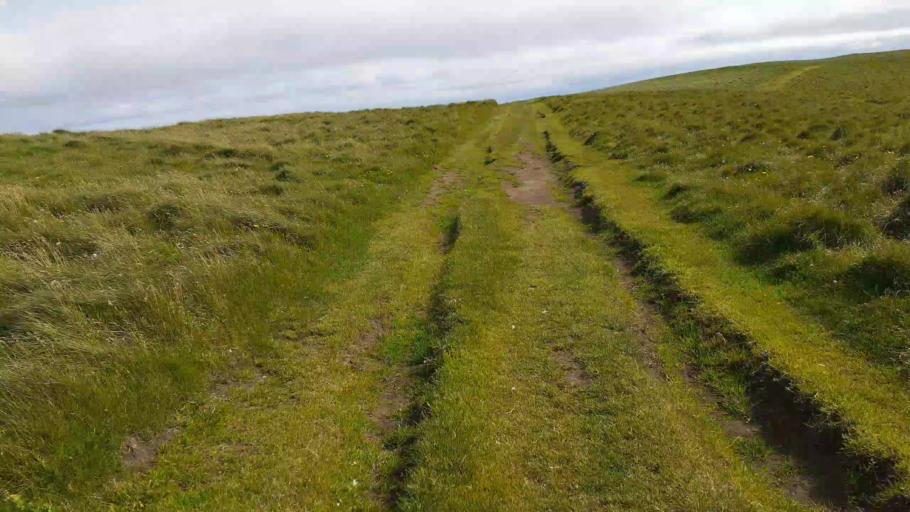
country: IS
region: Northeast
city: Dalvik
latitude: 66.5517
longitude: -17.9952
